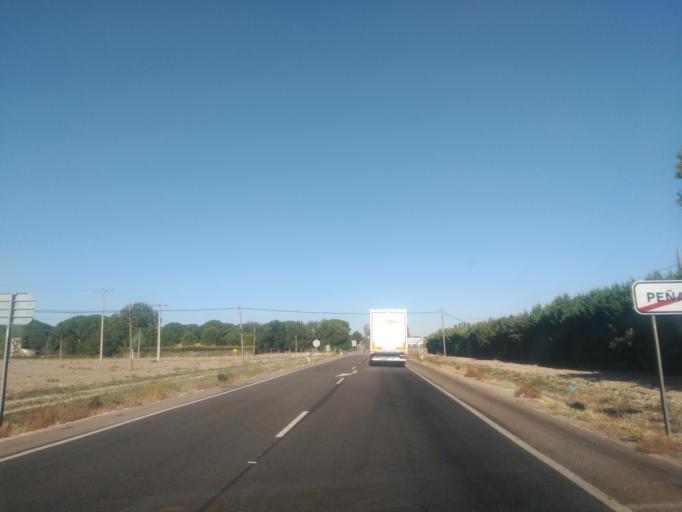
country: ES
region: Castille and Leon
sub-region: Provincia de Valladolid
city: Penafiel
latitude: 41.6023
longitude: -4.1357
